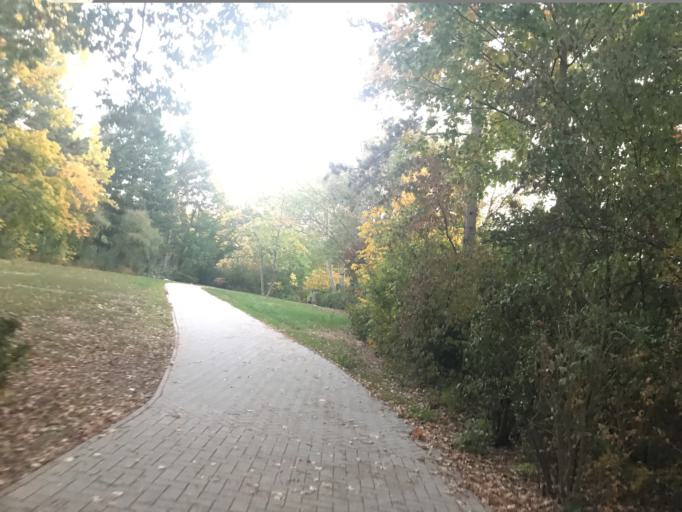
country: DE
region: Berlin
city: Britz
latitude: 52.4419
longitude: 13.4472
